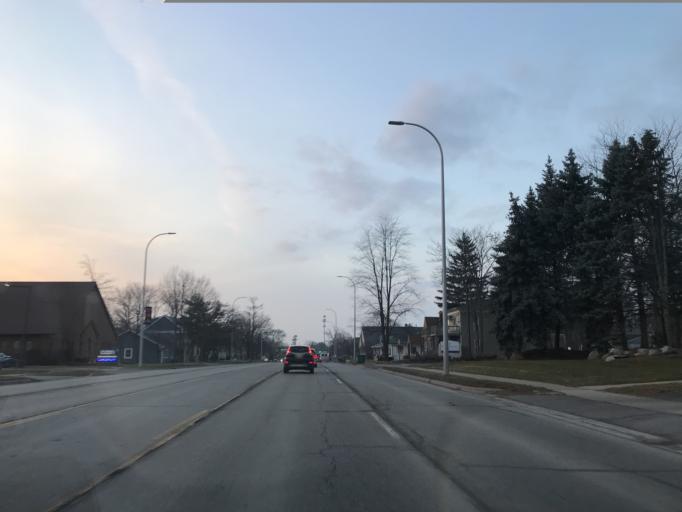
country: US
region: Michigan
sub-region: Livingston County
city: Brighton
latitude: 42.5242
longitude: -83.7734
